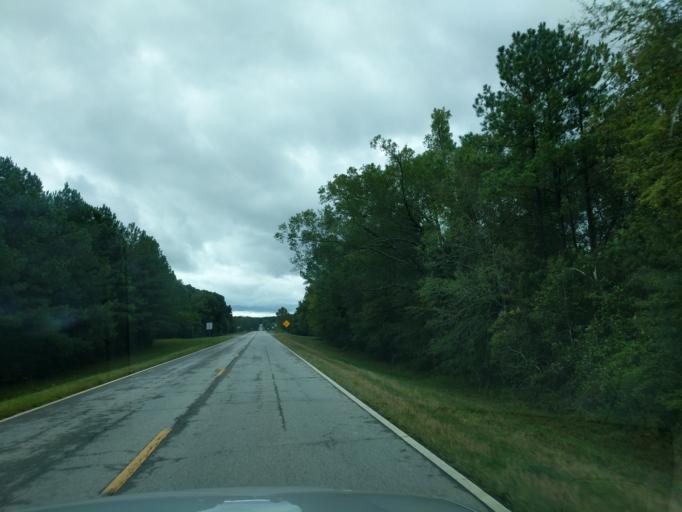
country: US
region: Georgia
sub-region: Elbert County
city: Elberton
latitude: 33.9764
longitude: -82.7723
